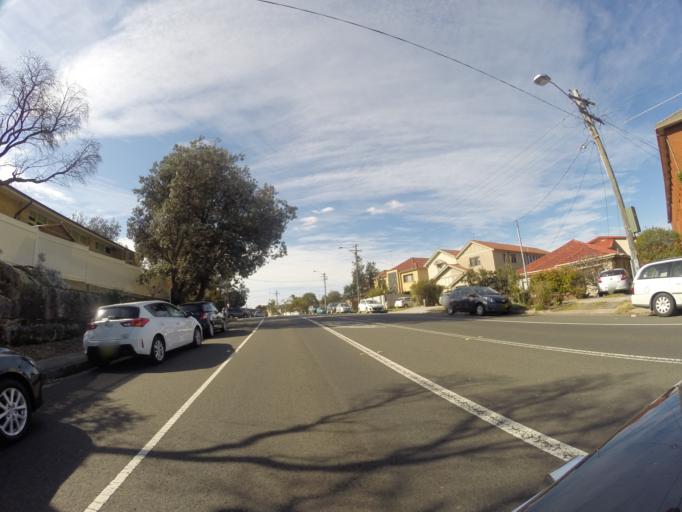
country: AU
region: New South Wales
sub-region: Randwick
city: South Coogee
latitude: -33.9399
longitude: 151.2560
